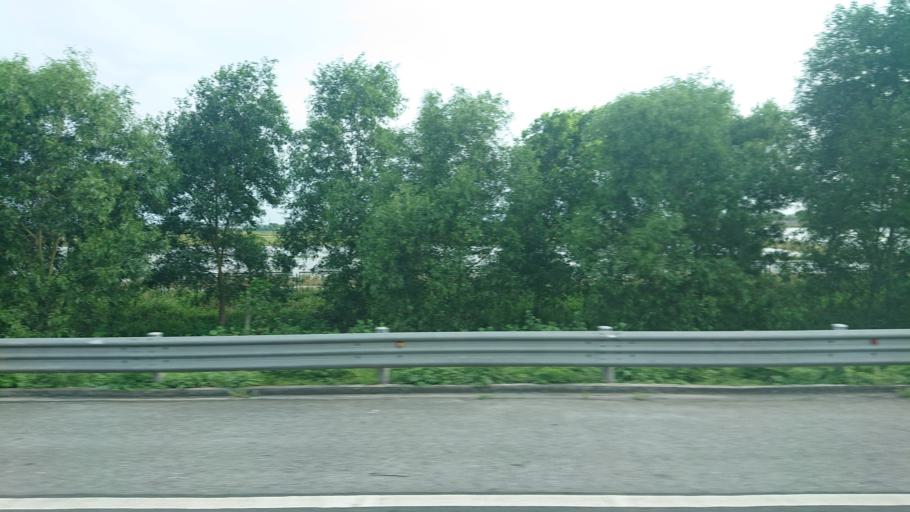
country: VN
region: Hai Phong
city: An Lao
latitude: 20.7969
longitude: 106.5418
